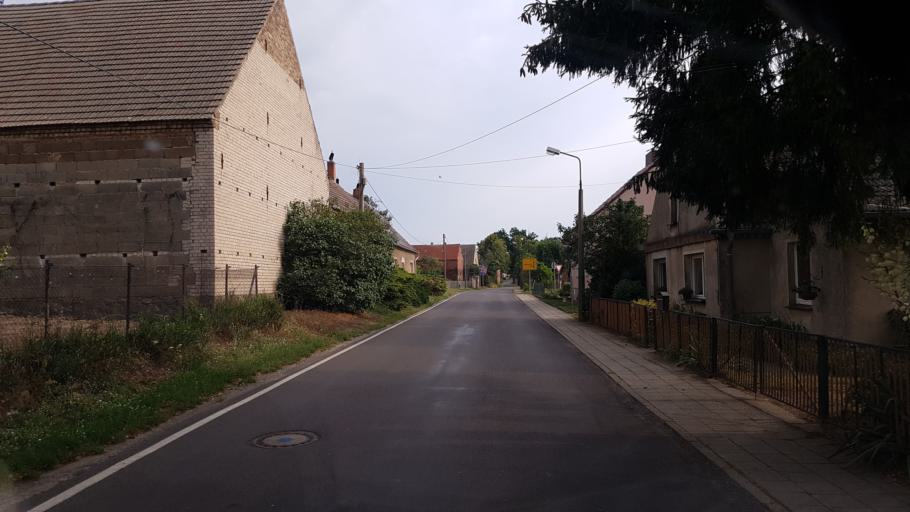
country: DE
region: Brandenburg
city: Dahme
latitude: 51.9439
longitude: 13.3956
